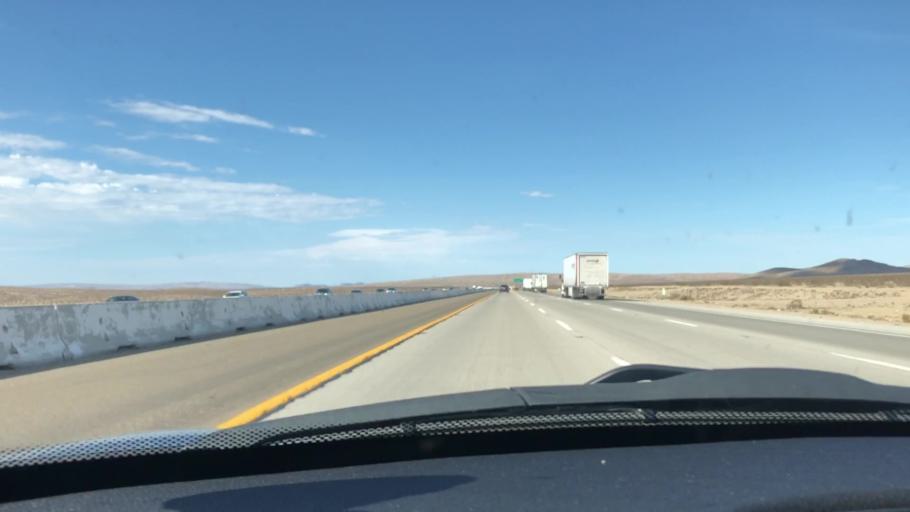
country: US
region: California
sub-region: San Bernardino County
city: Lenwood
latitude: 34.7947
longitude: -117.1150
